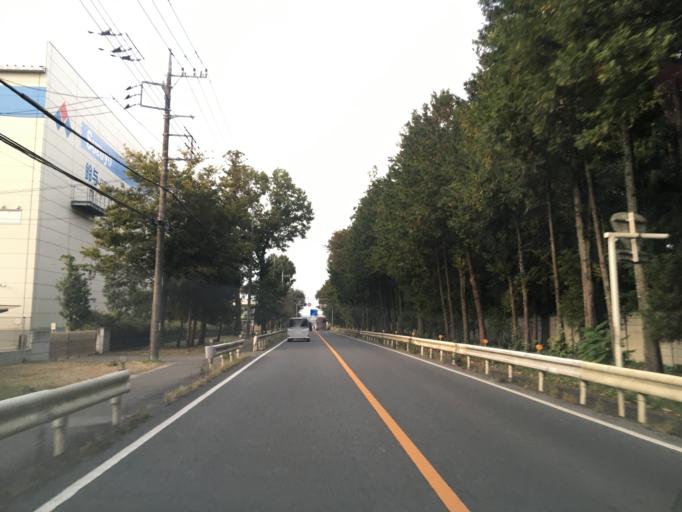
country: JP
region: Saitama
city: Sayama
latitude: 35.8917
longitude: 139.3782
